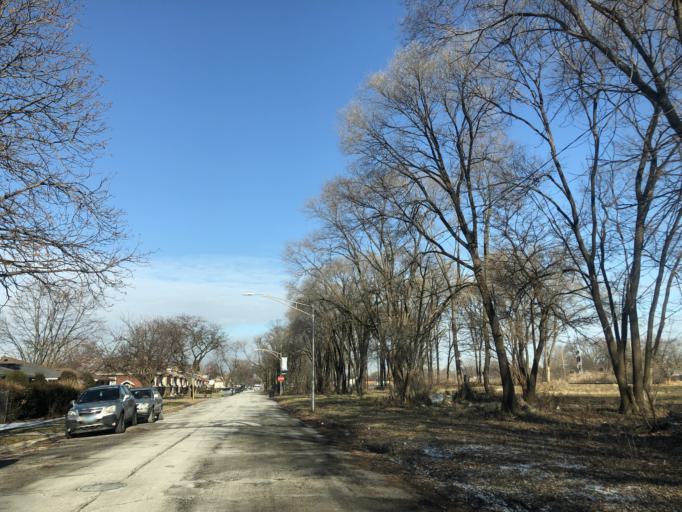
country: US
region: Illinois
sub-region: Cook County
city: Evergreen Park
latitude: 41.7603
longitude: -87.6794
